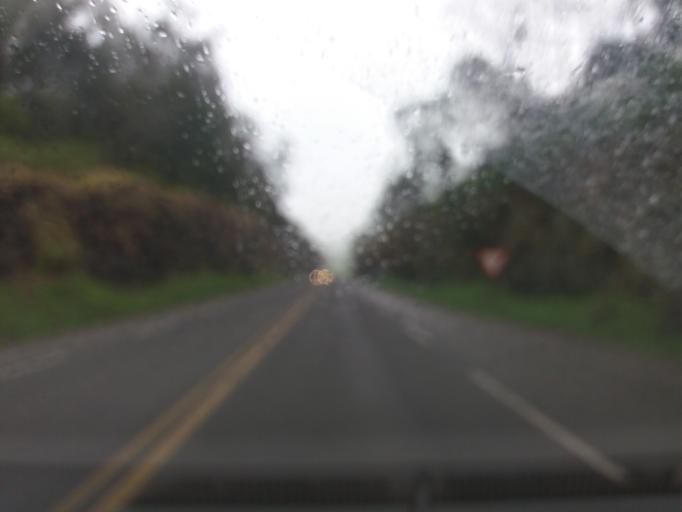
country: BR
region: Parana
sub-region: Francisco Beltrao
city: Francisco Beltrao
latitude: -26.0884
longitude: -53.2623
